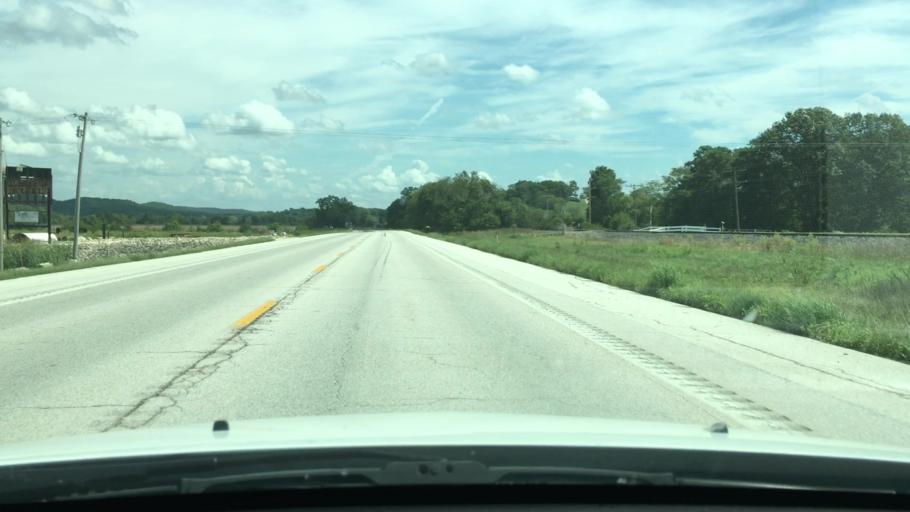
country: US
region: Missouri
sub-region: Pike County
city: Bowling Green
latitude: 39.3831
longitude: -91.1306
